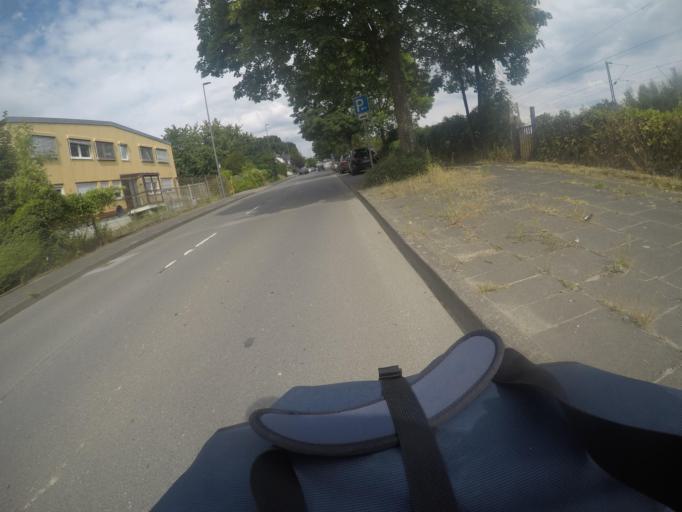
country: DE
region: North Rhine-Westphalia
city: Haan
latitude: 51.2271
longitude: 7.0547
